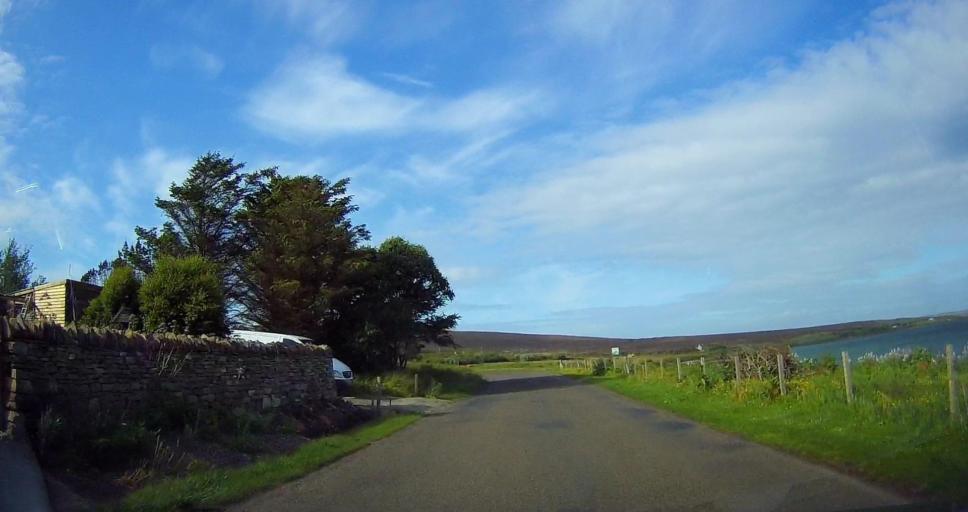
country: GB
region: Scotland
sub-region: Orkney Islands
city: Stromness
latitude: 58.7961
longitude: -3.2529
